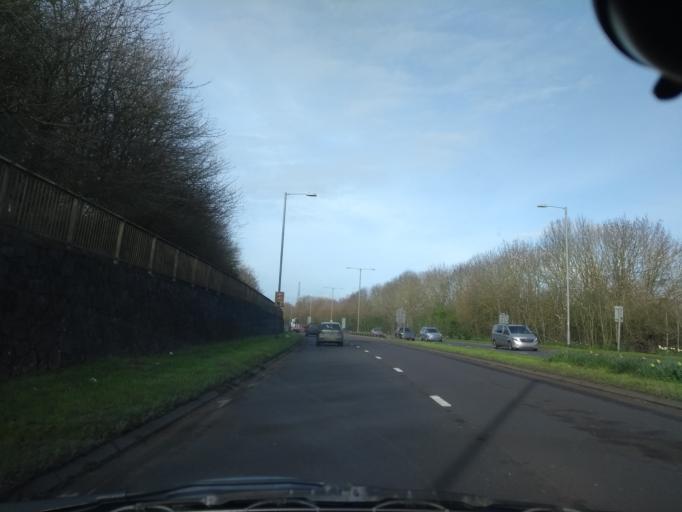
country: GB
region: England
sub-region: Somerset
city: Taunton
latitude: 51.0246
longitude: -3.0747
